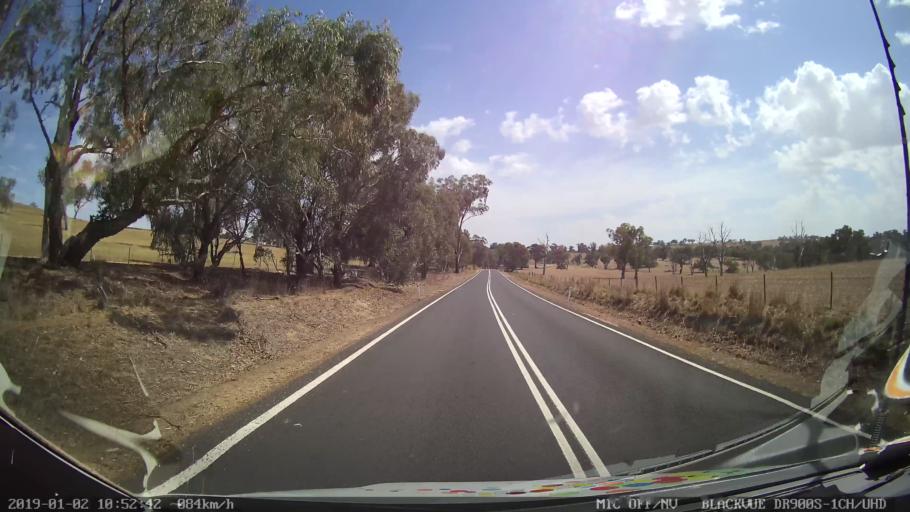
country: AU
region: New South Wales
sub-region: Cootamundra
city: Cootamundra
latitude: -34.6859
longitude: 148.2714
